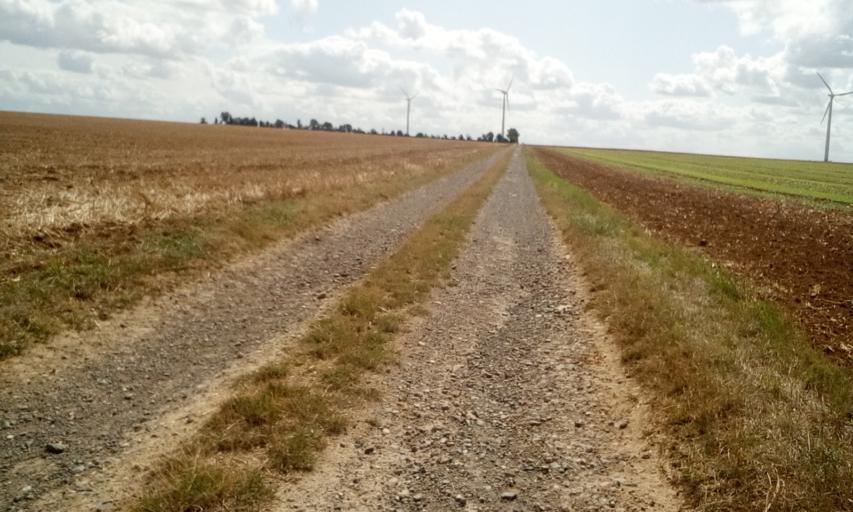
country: FR
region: Lower Normandy
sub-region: Departement du Calvados
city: Bellengreville
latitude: 49.1049
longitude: -0.2192
